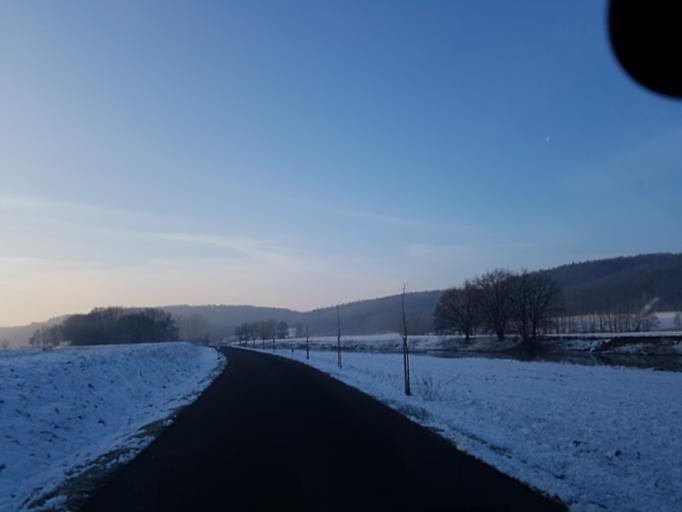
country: DE
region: Saxony
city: Grossweitzschen
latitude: 51.1519
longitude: 13.0100
